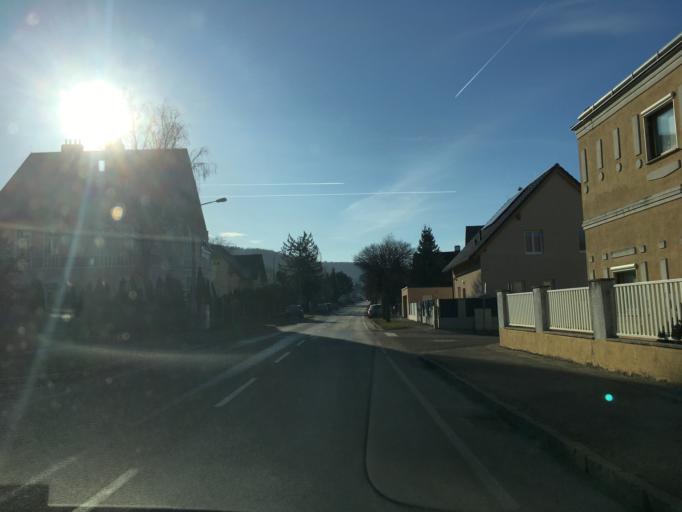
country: AT
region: Lower Austria
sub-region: Politischer Bezirk Tulln
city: Wordern
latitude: 48.3291
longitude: 16.2192
